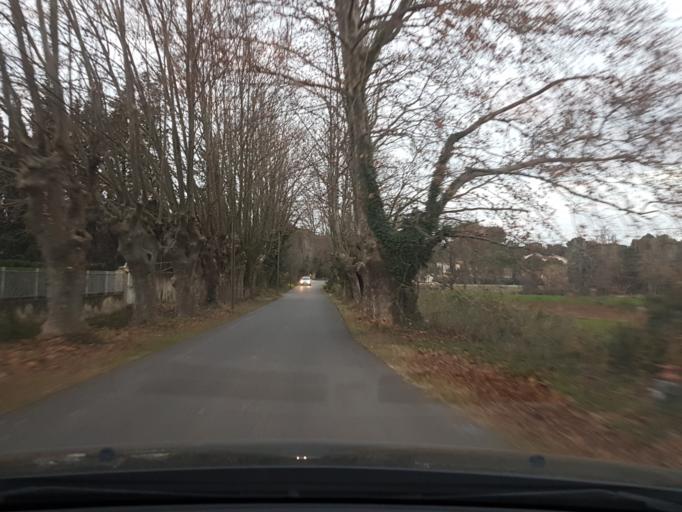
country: FR
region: Provence-Alpes-Cote d'Azur
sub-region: Departement du Vaucluse
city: Loriol-du-Comtat
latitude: 44.0807
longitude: 4.9988
